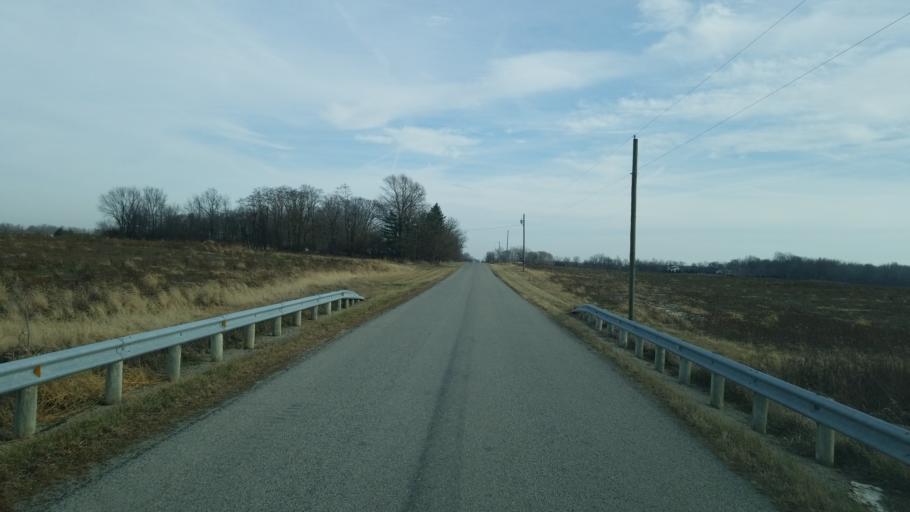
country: US
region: Ohio
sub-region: Union County
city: Richwood
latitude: 40.4404
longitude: -83.4286
